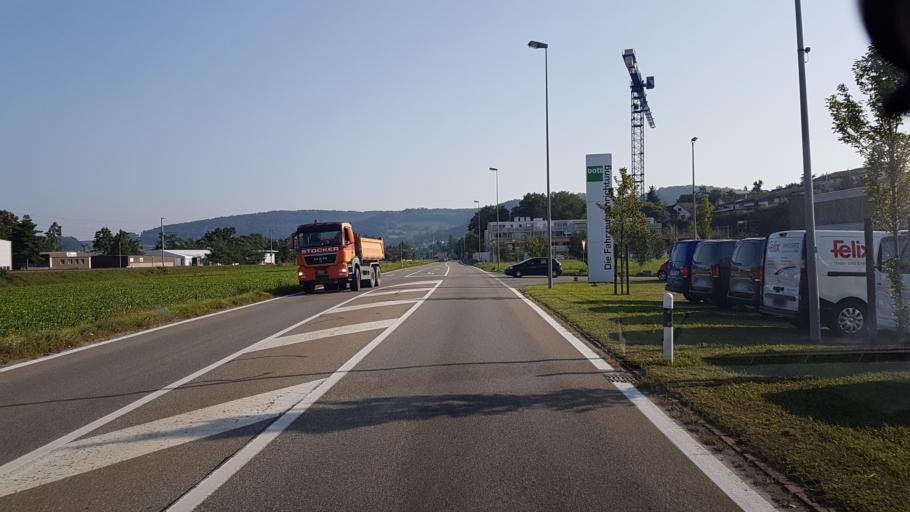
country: CH
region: Aargau
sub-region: Bezirk Zurzach
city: Klingnau
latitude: 47.5585
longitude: 8.2508
